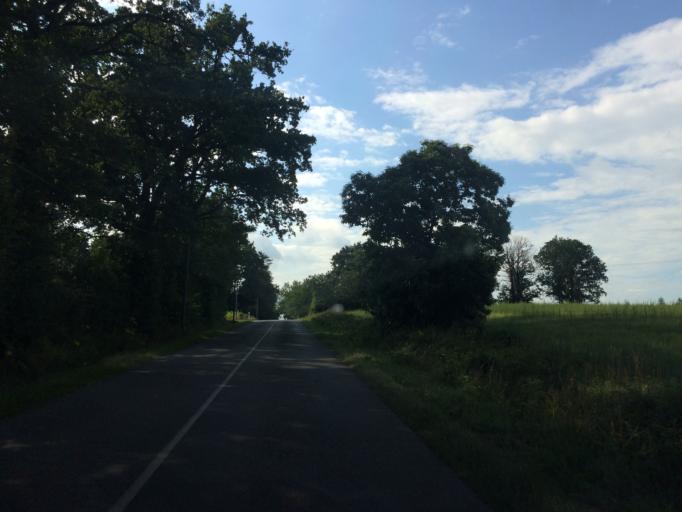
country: FR
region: Pays de la Loire
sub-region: Departement de la Loire-Atlantique
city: Avessac
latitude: 47.6312
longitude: -1.9530
